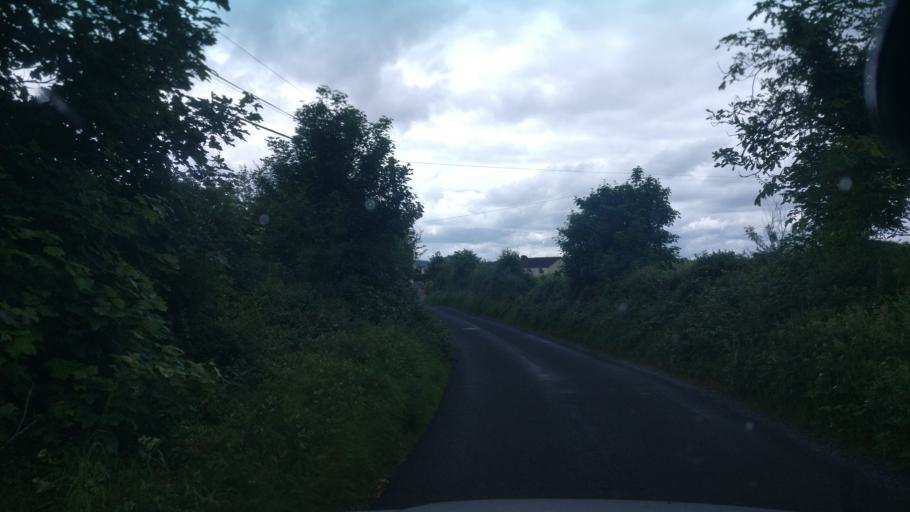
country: IE
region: Connaught
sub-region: County Galway
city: Loughrea
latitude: 53.1729
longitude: -8.5685
